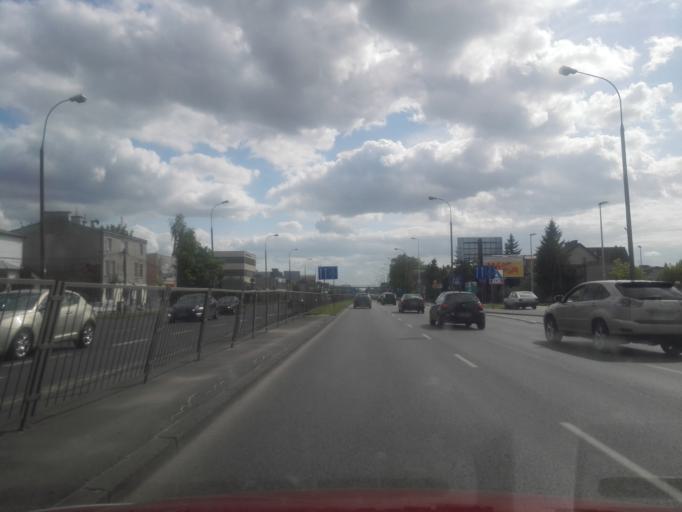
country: PL
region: Masovian Voivodeship
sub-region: Warszawa
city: Targowek
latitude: 52.2866
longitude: 21.0750
